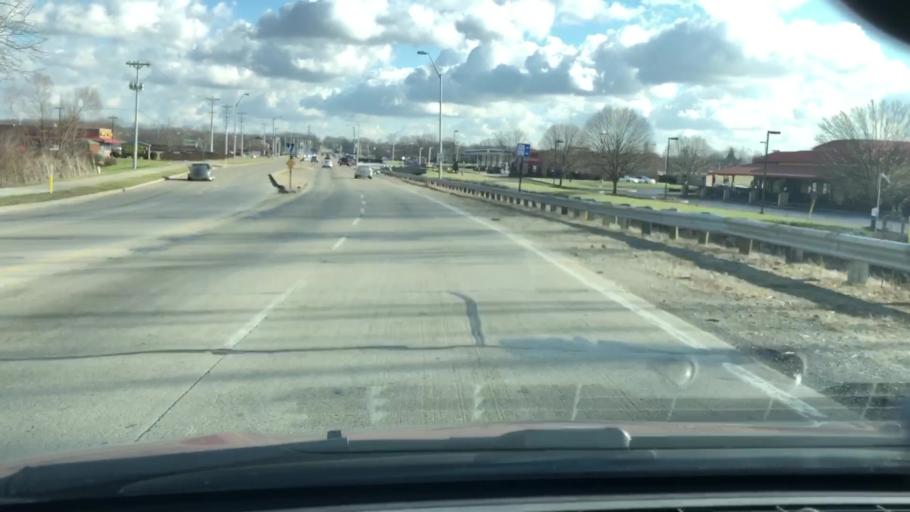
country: US
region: Ohio
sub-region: Greene County
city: Fairborn
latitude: 39.7829
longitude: -84.0004
